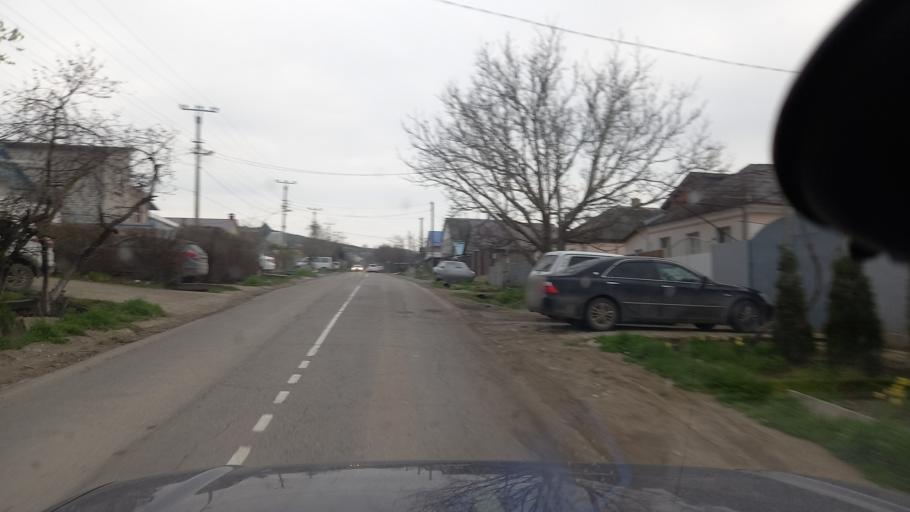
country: RU
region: Krasnodarskiy
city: Sukko
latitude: 44.8525
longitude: 37.4366
